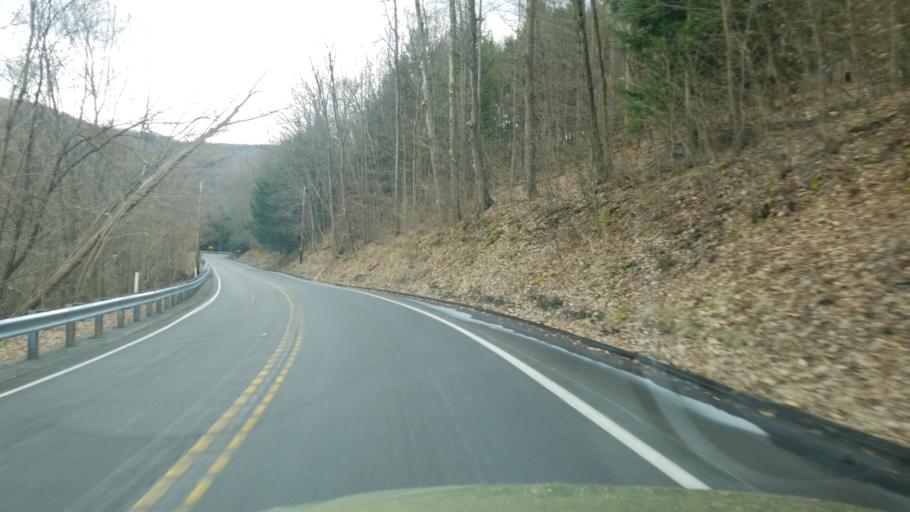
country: US
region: Pennsylvania
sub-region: Clearfield County
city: Curwensville
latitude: 40.8672
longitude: -78.4477
